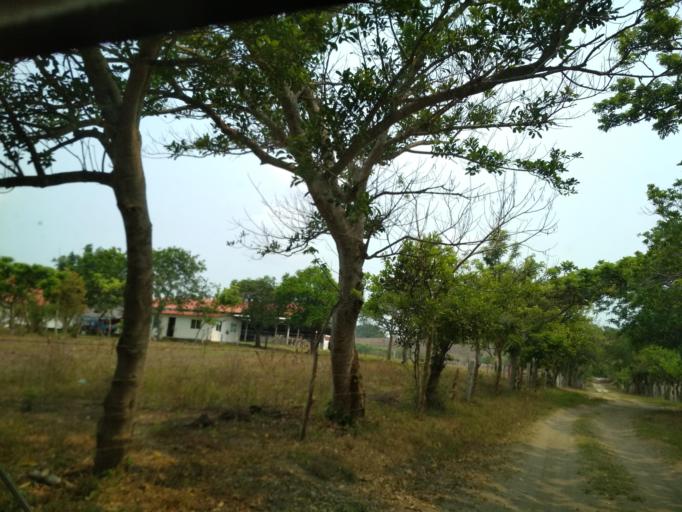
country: MX
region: Veracruz
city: Anton Lizardo
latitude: 19.0157
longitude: -95.9886
